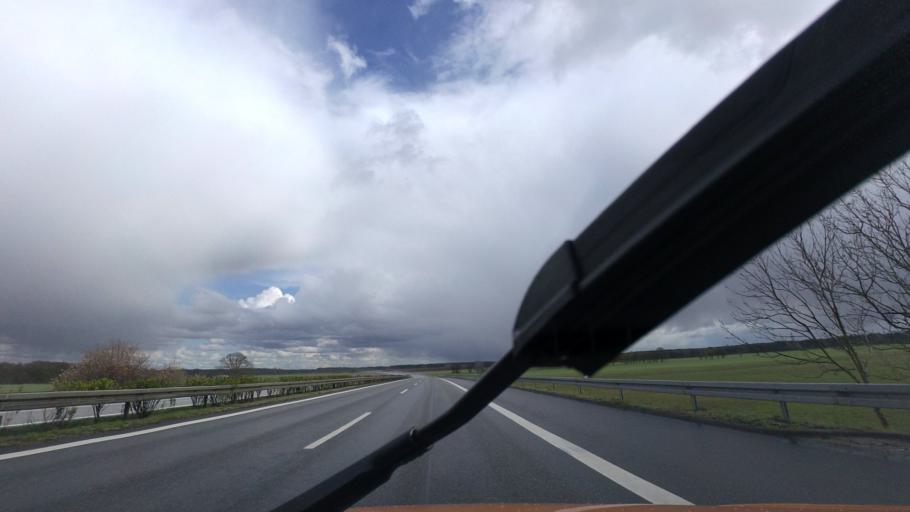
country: DE
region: Mecklenburg-Vorpommern
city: Sulstorf
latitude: 53.4771
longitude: 11.2976
